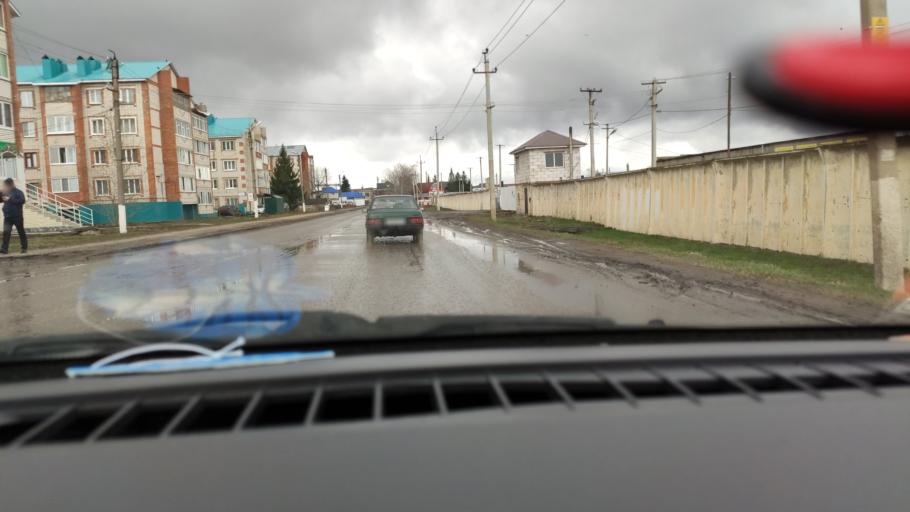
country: RU
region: Tatarstan
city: Nurlat
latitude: 54.4240
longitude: 50.7901
